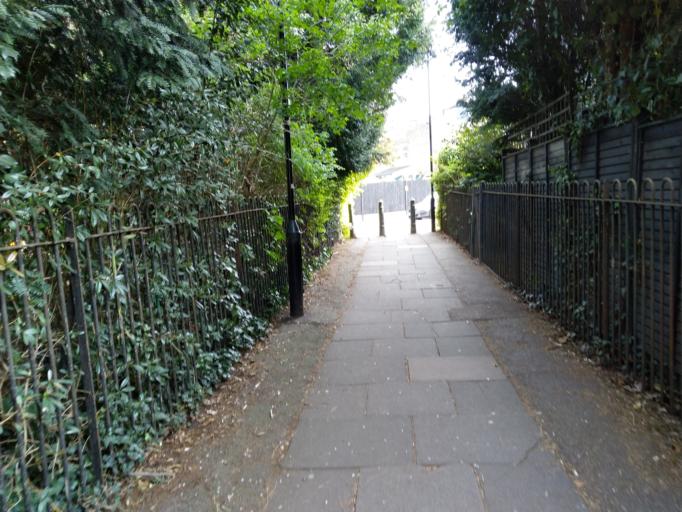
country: GB
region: England
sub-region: Greater London
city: Crouch End
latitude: 51.5854
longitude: -0.1279
